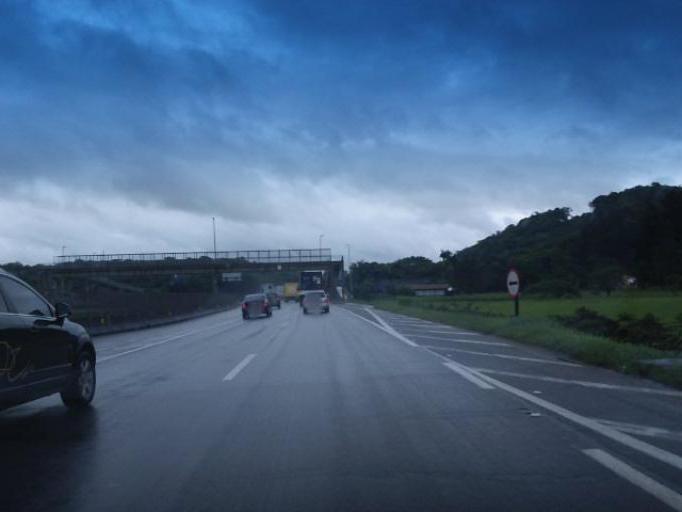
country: BR
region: Santa Catarina
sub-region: Balneario Camboriu
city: Balneario Camboriu
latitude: -26.9815
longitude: -48.6761
